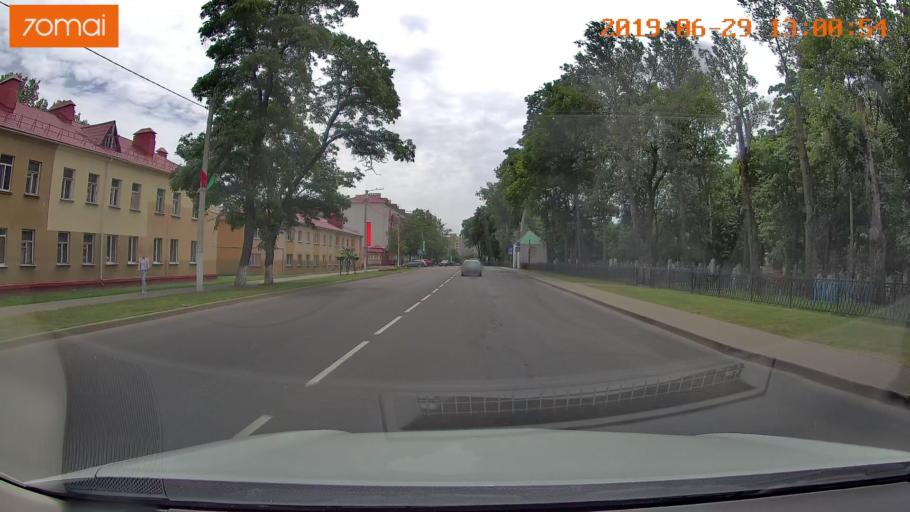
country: BY
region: Minsk
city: Slutsk
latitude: 53.0417
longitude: 27.5585
